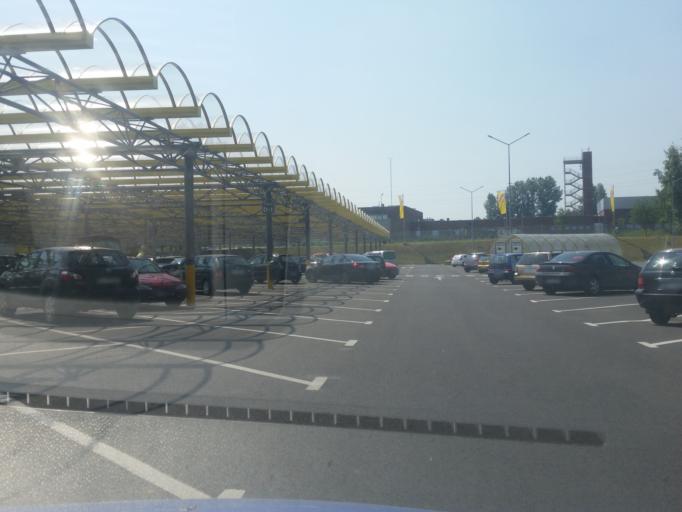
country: PL
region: Silesian Voivodeship
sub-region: Sosnowiec
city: Sosnowiec
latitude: 50.2568
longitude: 19.0901
